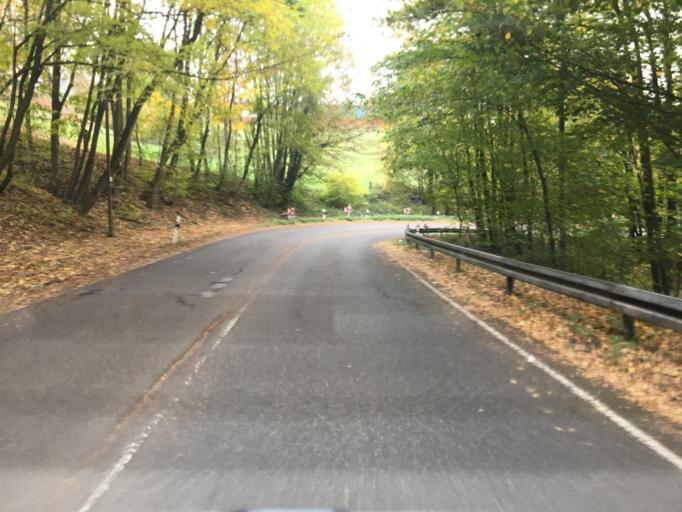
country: DE
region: North Rhine-Westphalia
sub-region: Regierungsbezirk Dusseldorf
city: Velbert
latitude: 51.3314
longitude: 7.0696
